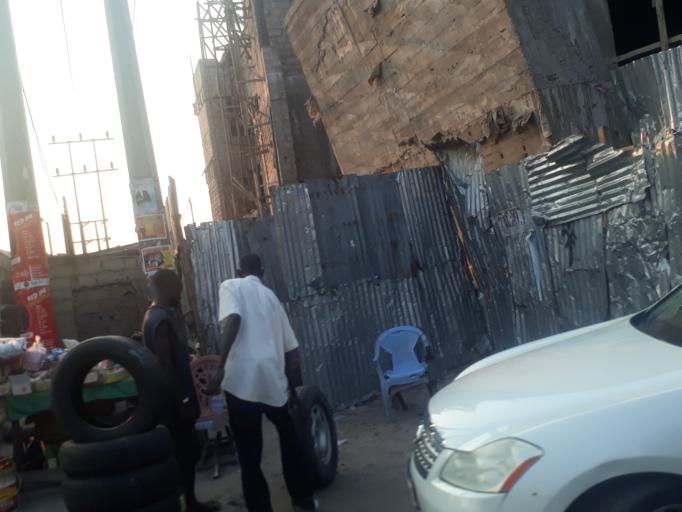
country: CD
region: Kinshasa
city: Kinshasa
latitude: -4.3377
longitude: 15.3051
